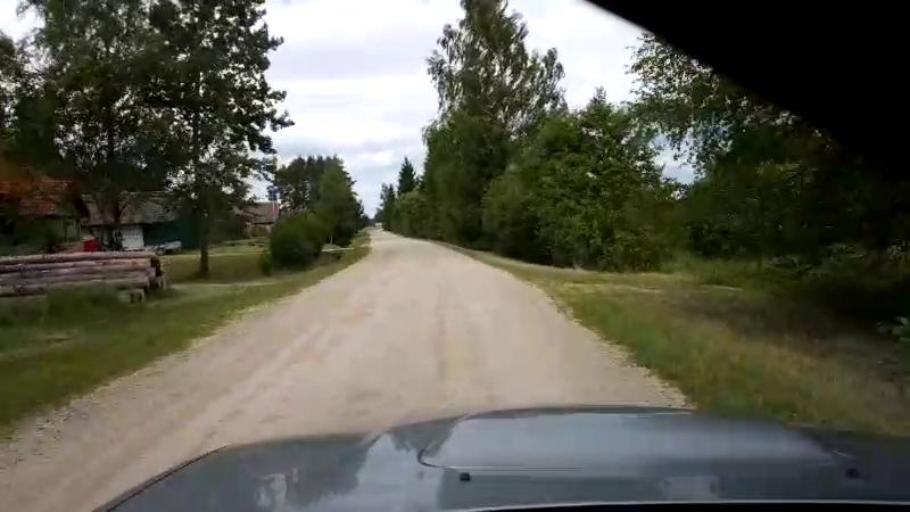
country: EE
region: Paernumaa
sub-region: Halinga vald
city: Parnu-Jaagupi
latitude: 58.5240
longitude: 24.5859
